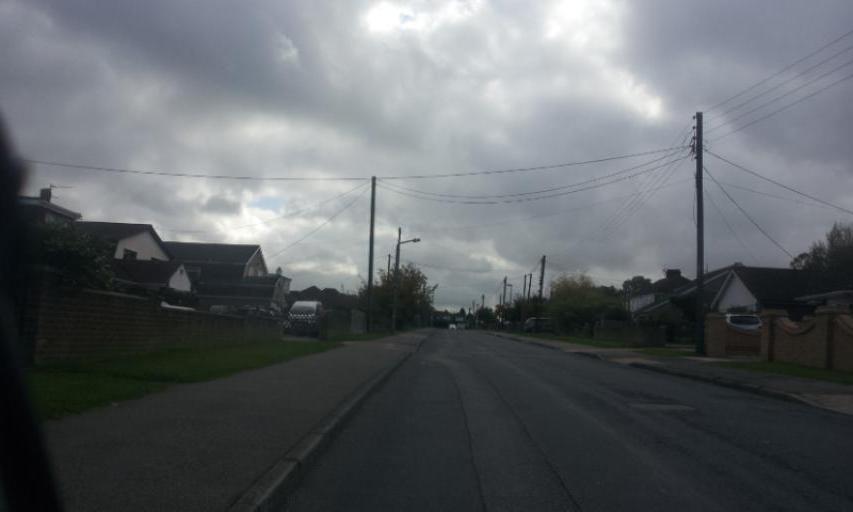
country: GB
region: England
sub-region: Kent
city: Chatham
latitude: 51.3414
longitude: 0.5183
